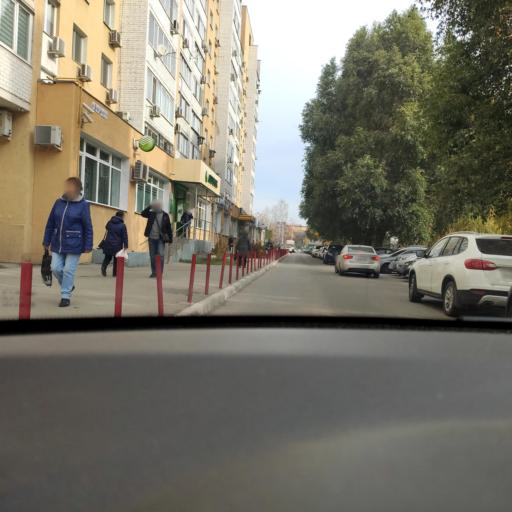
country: RU
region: Samara
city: Samara
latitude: 53.2475
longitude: 50.2376
